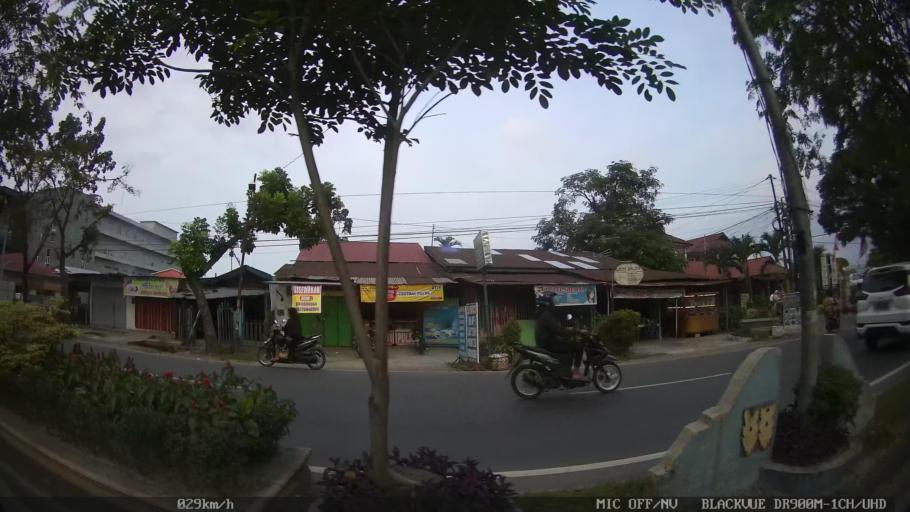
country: ID
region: North Sumatra
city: Sunggal
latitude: 3.5816
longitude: 98.6152
